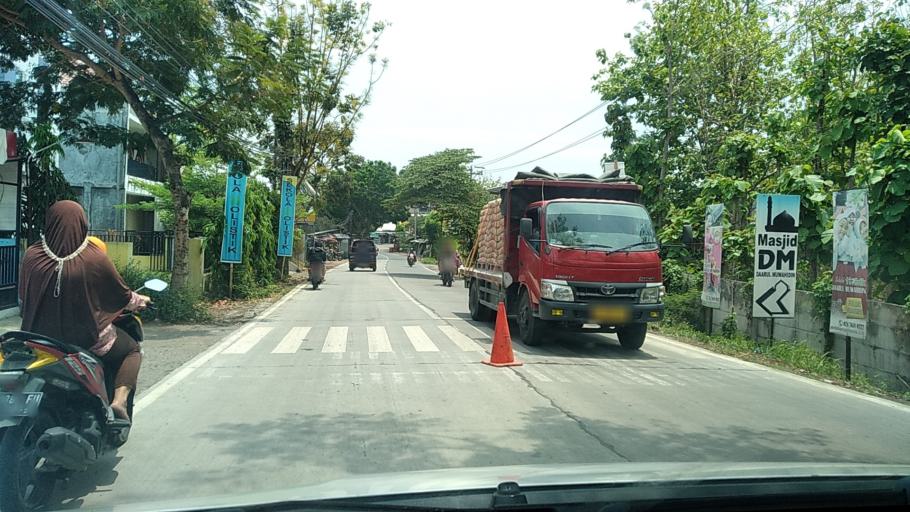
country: ID
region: Central Java
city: Mranggen
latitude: -7.0408
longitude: 110.4676
